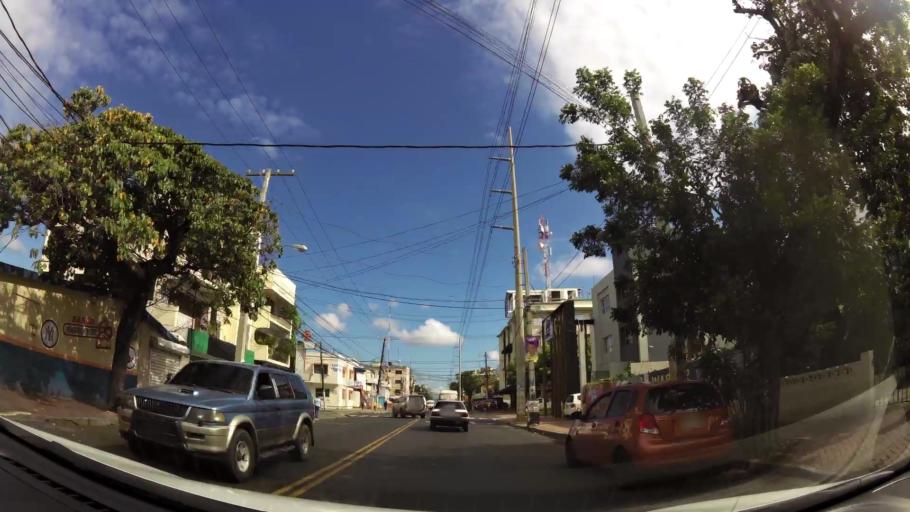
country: DO
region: Santo Domingo
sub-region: Santo Domingo
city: Santo Domingo Este
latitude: 18.4888
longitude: -69.8654
